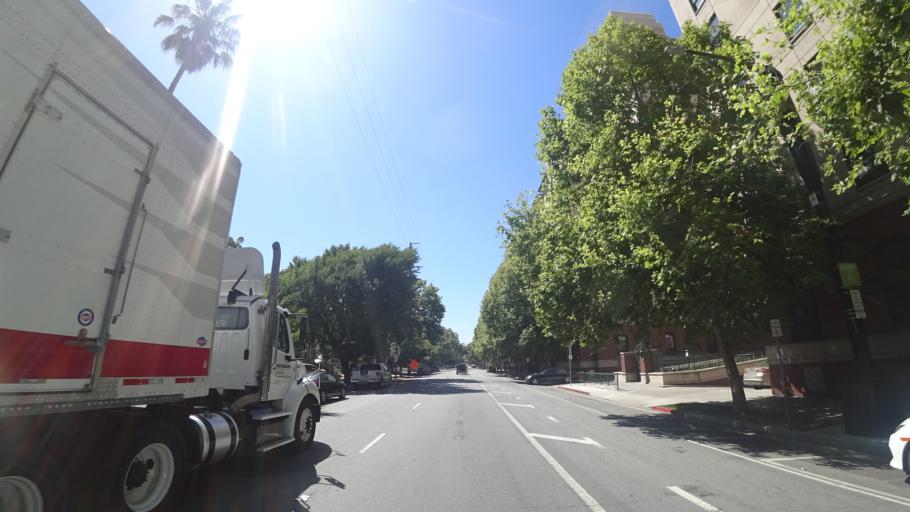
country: US
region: California
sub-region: Santa Clara County
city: San Jose
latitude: 37.3356
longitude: -121.8773
